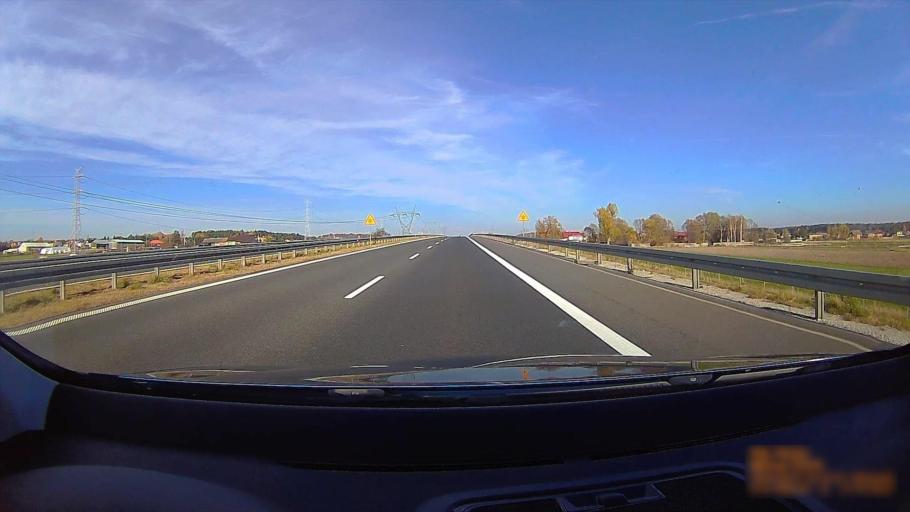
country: PL
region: Greater Poland Voivodeship
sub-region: Powiat ostrowski
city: Przygodzice
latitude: 51.6026
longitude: 17.8531
